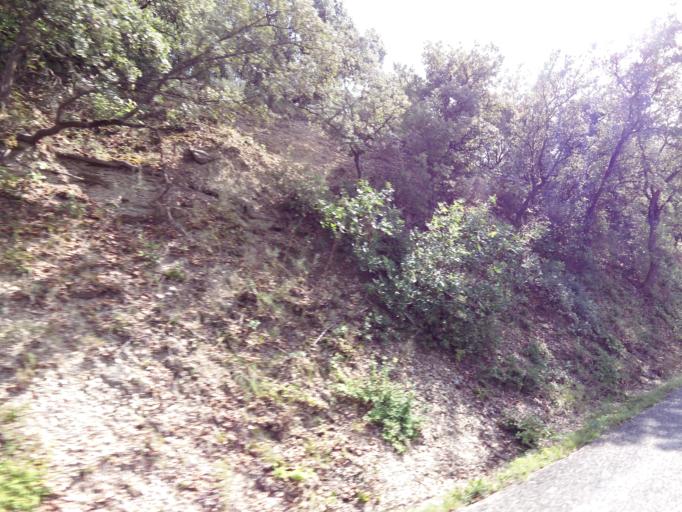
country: FR
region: Languedoc-Roussillon
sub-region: Departement du Gard
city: Villevieille
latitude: 43.7976
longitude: 4.1036
